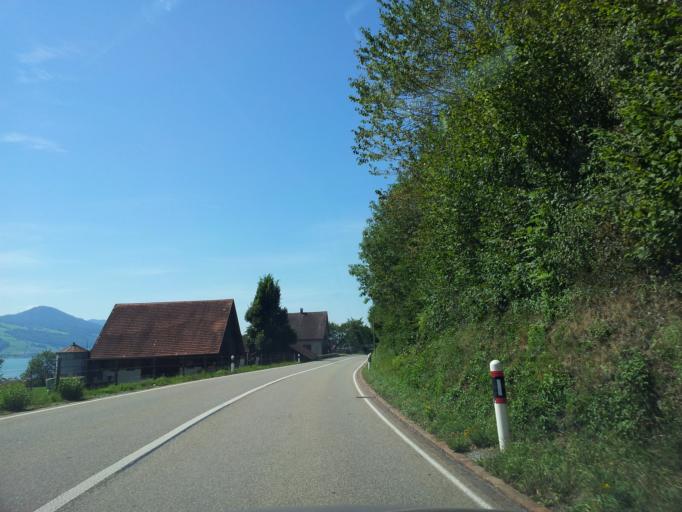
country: CH
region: Schwyz
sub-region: Bezirk March
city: Lachen
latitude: 47.2184
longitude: 8.8794
